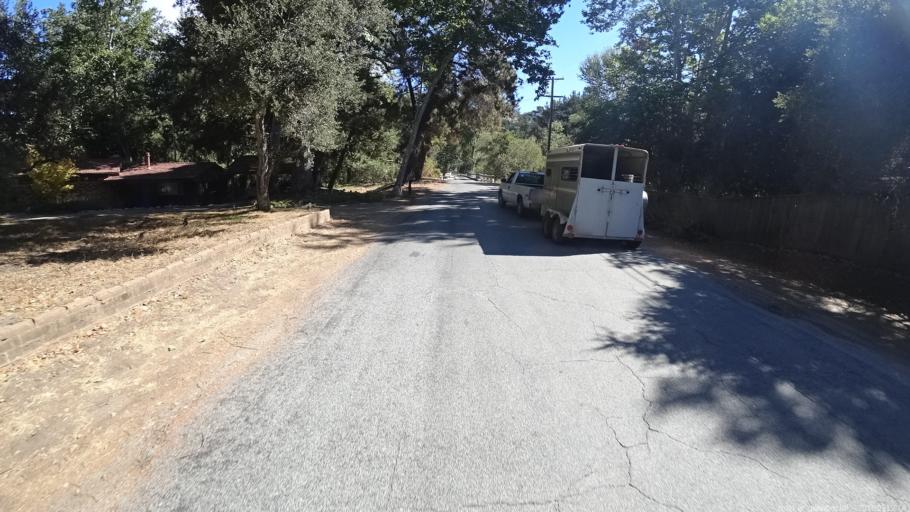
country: US
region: California
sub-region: Monterey County
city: Carmel Valley Village
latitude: 36.4896
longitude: -121.7493
